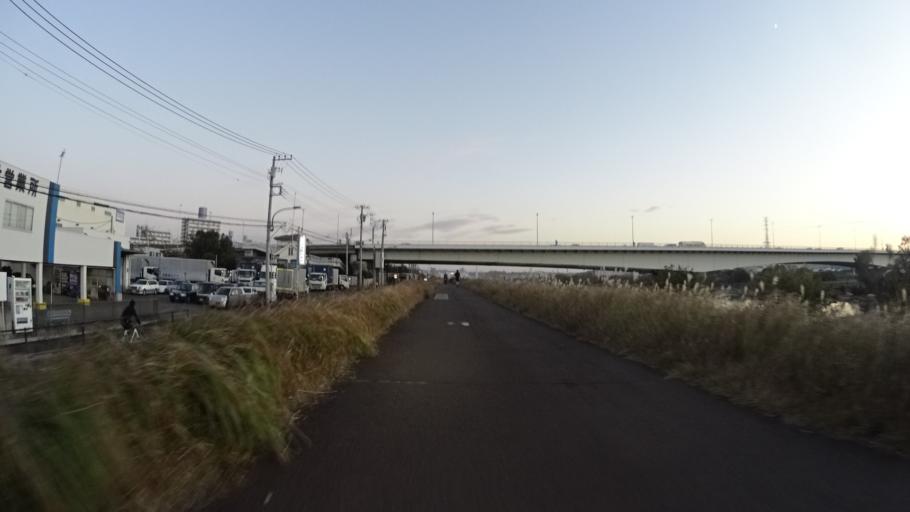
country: JP
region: Tokyo
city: Hino
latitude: 35.6753
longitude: 139.4271
